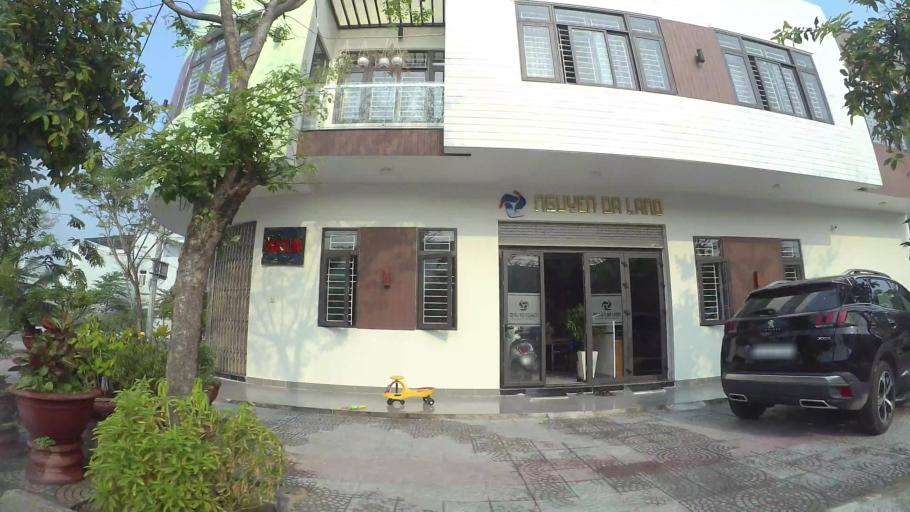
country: VN
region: Da Nang
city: Cam Le
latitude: 16.0060
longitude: 108.2240
